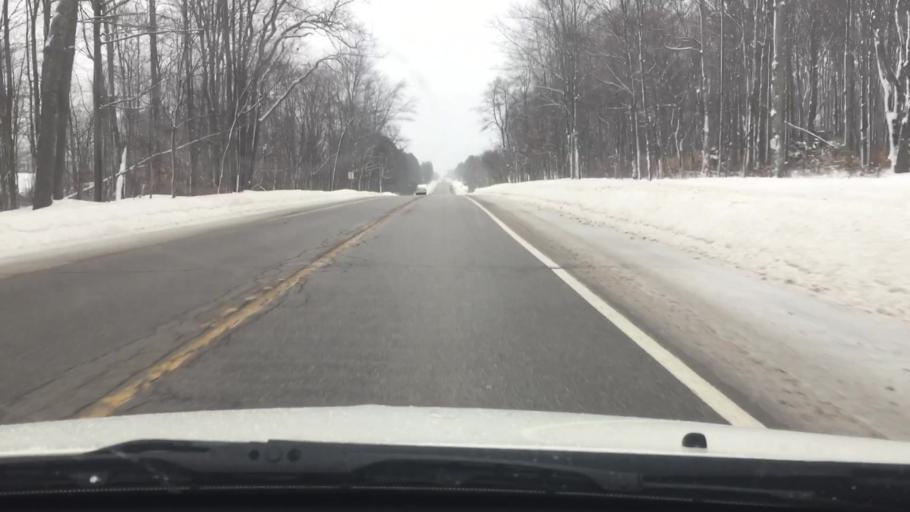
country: US
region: Michigan
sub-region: Otsego County
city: Gaylord
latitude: 45.0360
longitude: -84.7758
